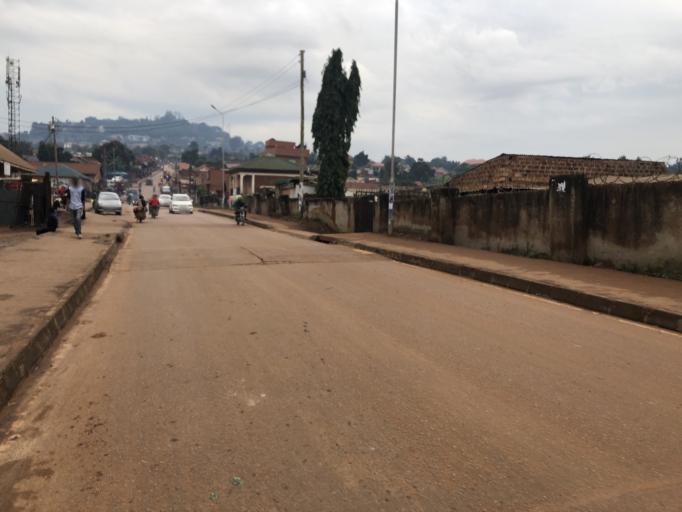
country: UG
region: Central Region
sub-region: Kampala District
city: Kampala
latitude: 0.2832
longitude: 32.6039
